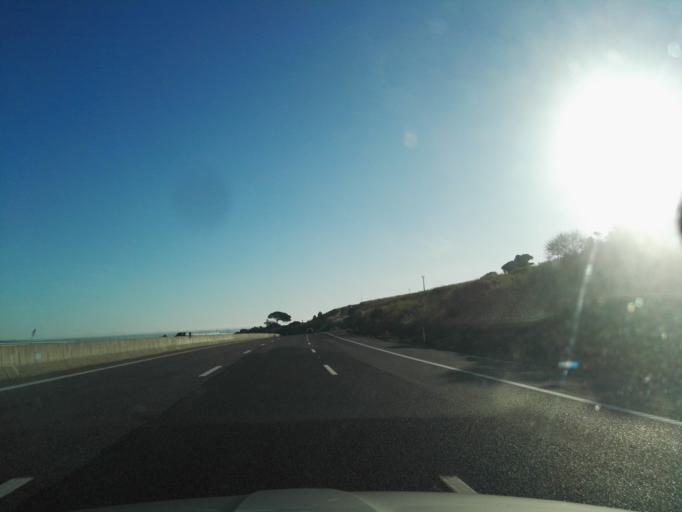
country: PT
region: Lisbon
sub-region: Alenquer
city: Carregado
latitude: 39.0118
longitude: -8.9985
